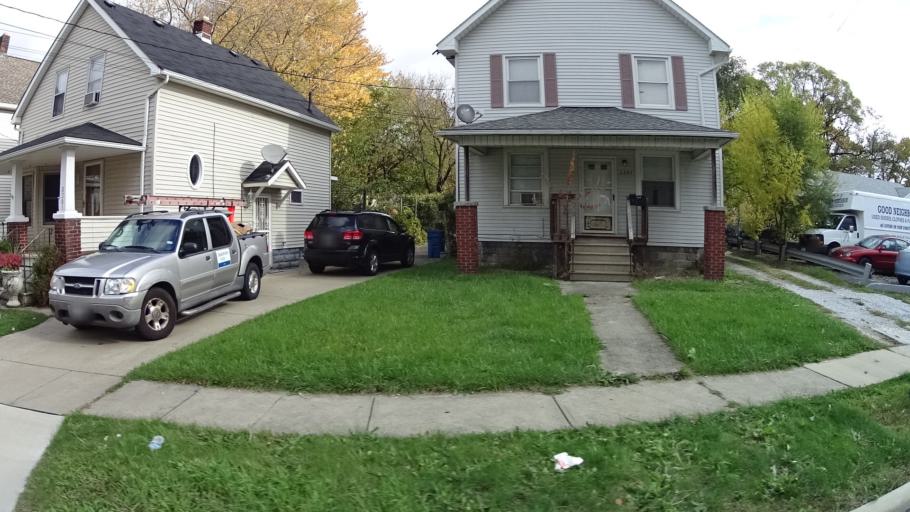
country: US
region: Ohio
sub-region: Lorain County
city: Lorain
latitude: 41.4481
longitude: -82.1626
